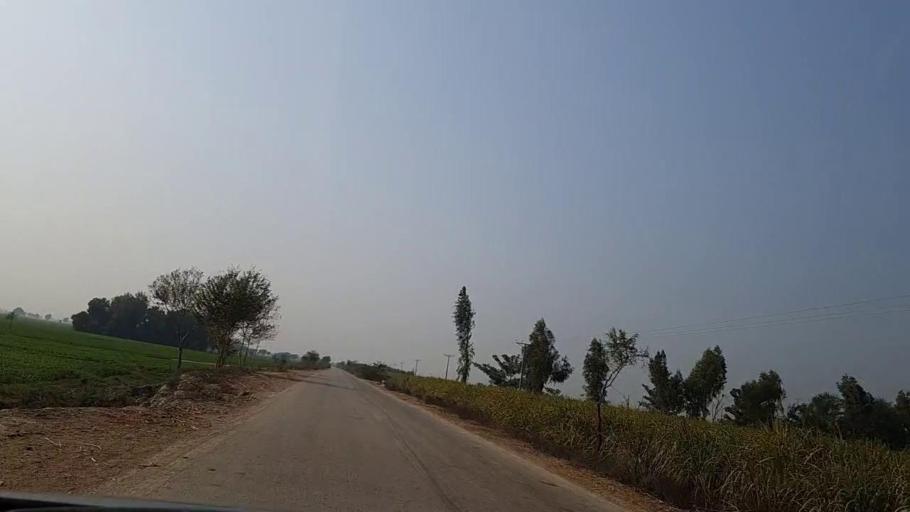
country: PK
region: Sindh
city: Sann
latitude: 26.1383
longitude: 68.1711
